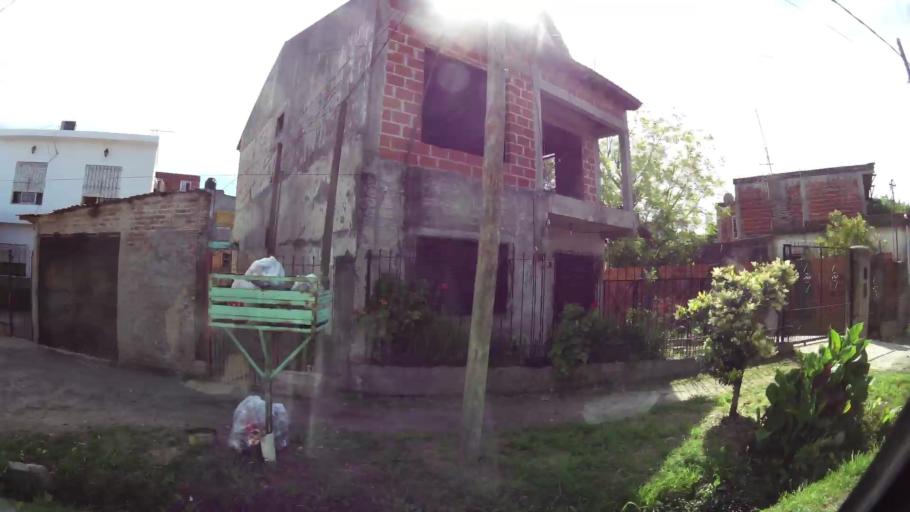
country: AR
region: Buenos Aires
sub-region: Partido de Quilmes
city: Quilmes
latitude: -34.7781
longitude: -58.3021
